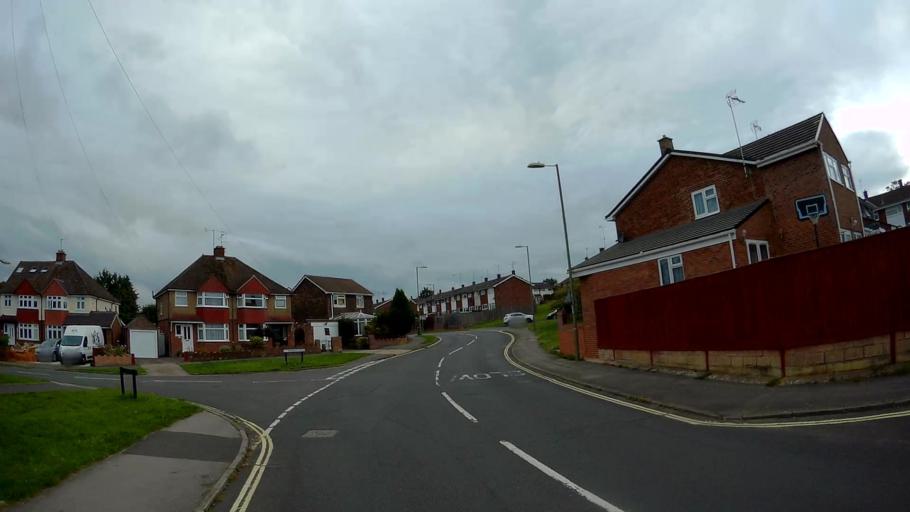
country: GB
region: England
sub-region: Hampshire
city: Basingstoke
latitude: 51.2618
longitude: -1.0949
